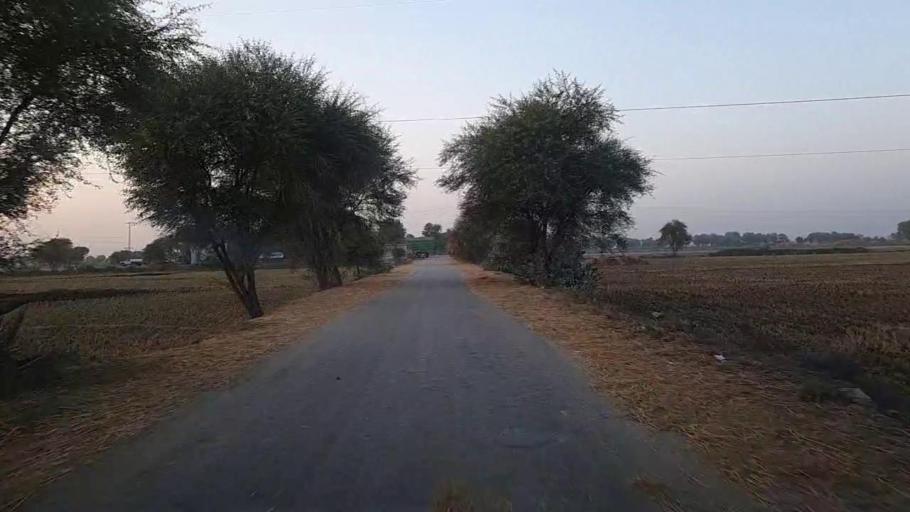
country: PK
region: Sindh
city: Kashmor
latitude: 28.4166
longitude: 69.4509
